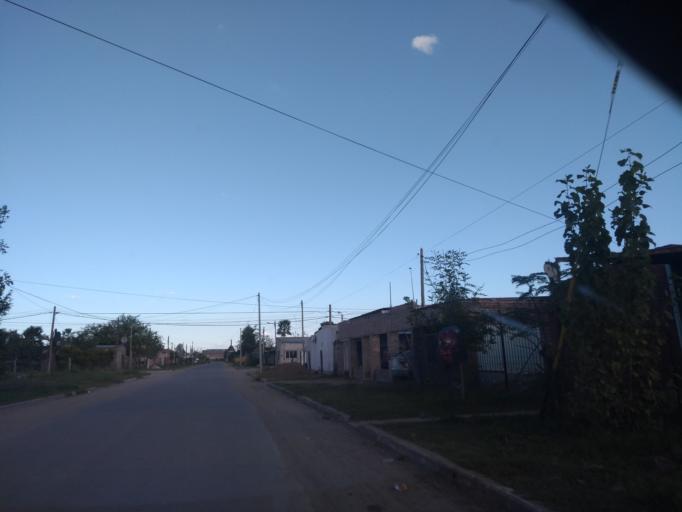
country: AR
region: Chaco
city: Barranqueras
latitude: -27.4912
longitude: -58.9374
